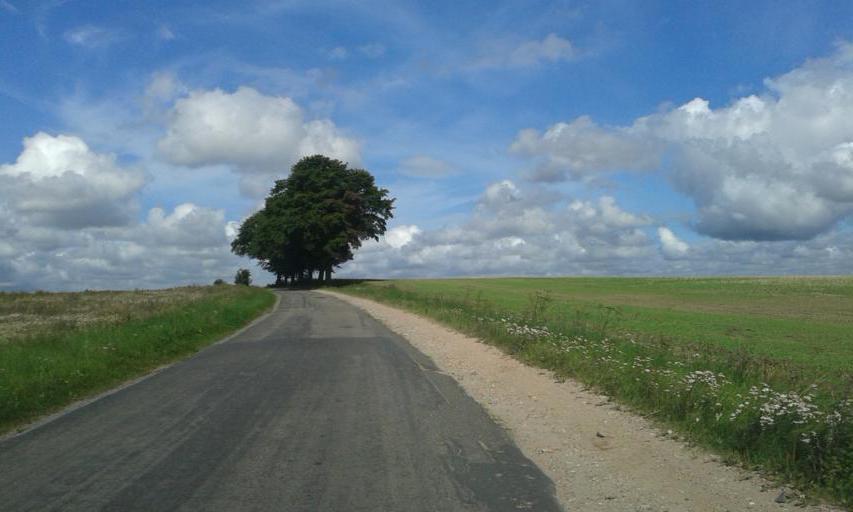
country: PL
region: West Pomeranian Voivodeship
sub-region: Powiat slawienski
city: Slawno
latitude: 54.2979
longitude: 16.6420
